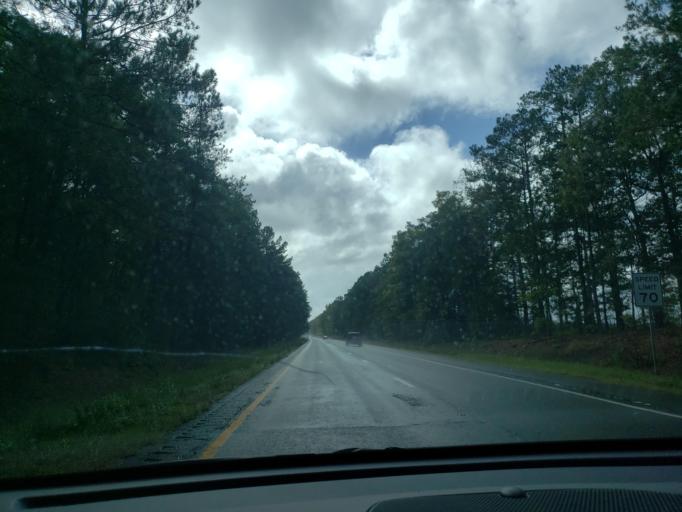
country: US
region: Virginia
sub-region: Dinwiddie County
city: Dinwiddie
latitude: 37.0278
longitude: -77.6413
